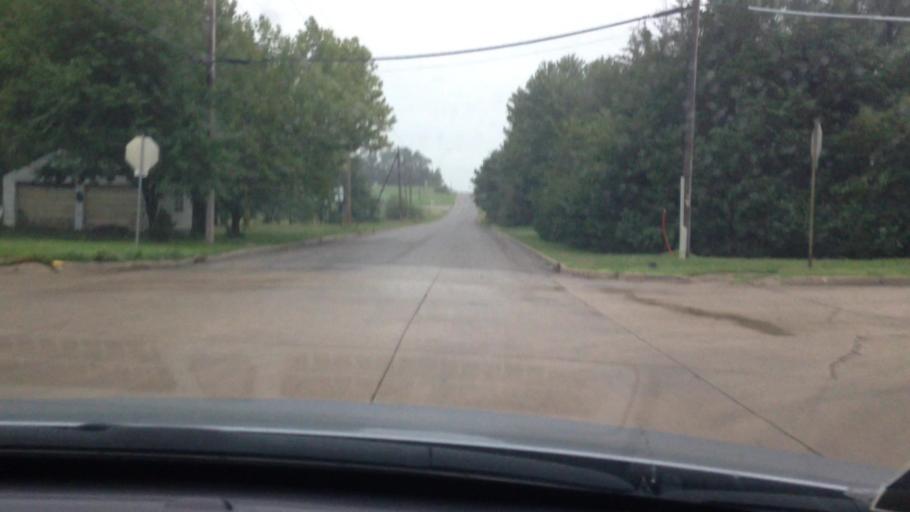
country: US
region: Kansas
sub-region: Brown County
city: Hiawatha
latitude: 39.8488
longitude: -95.5459
